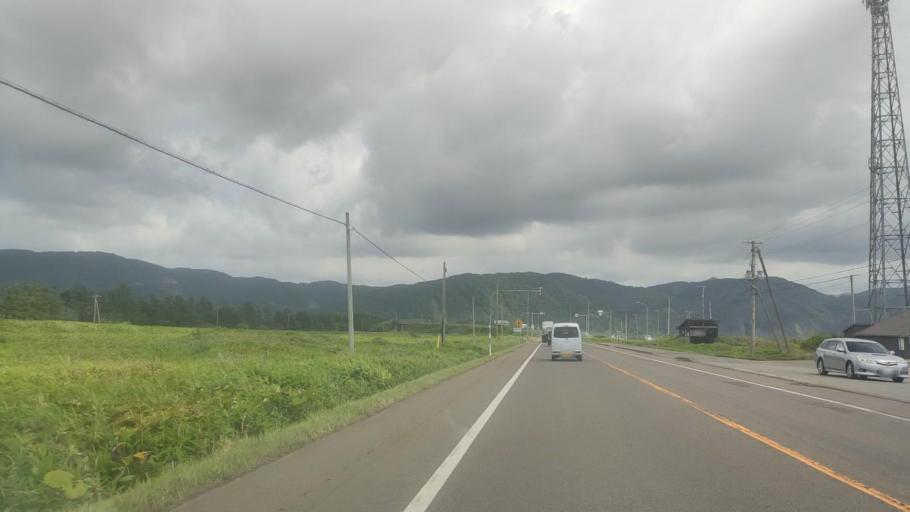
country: JP
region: Hokkaido
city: Niseko Town
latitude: 42.5764
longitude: 140.4513
